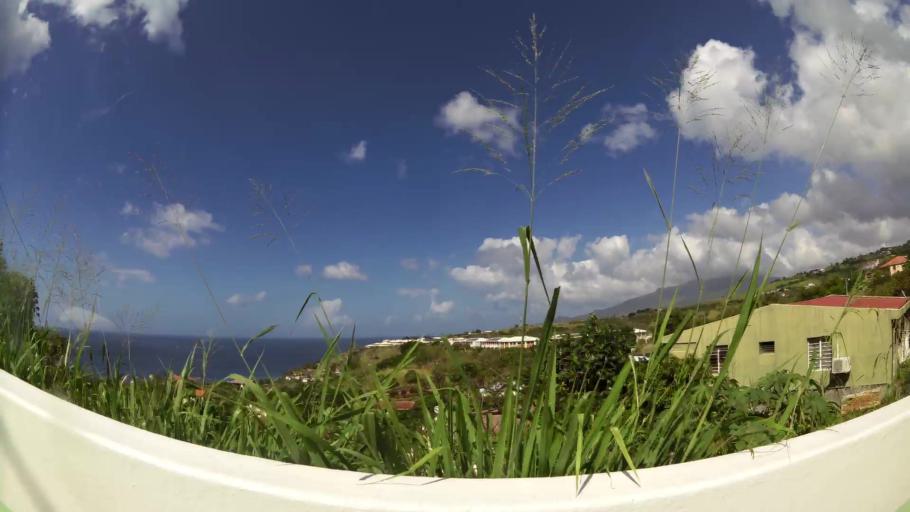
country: MQ
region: Martinique
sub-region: Martinique
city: Saint-Pierre
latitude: 14.6950
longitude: -61.1740
